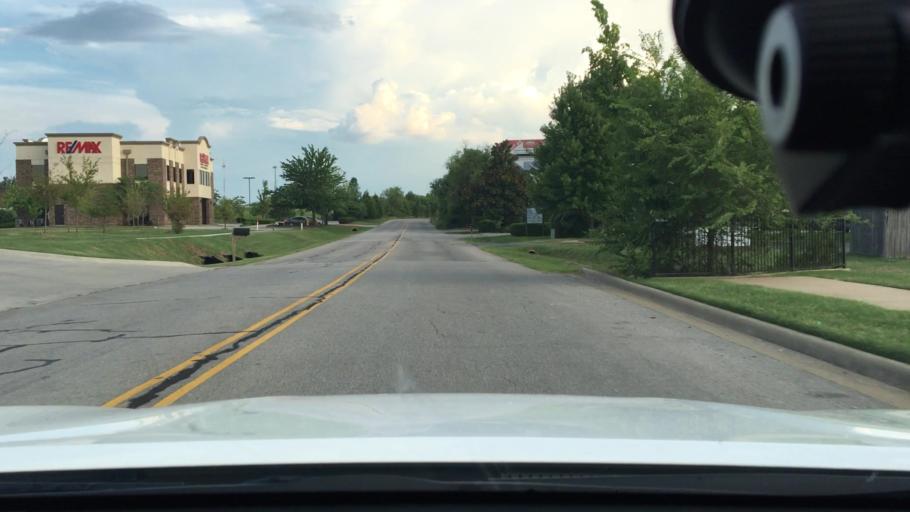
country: US
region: Arkansas
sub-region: Benton County
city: Bentonville
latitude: 36.3387
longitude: -94.1839
